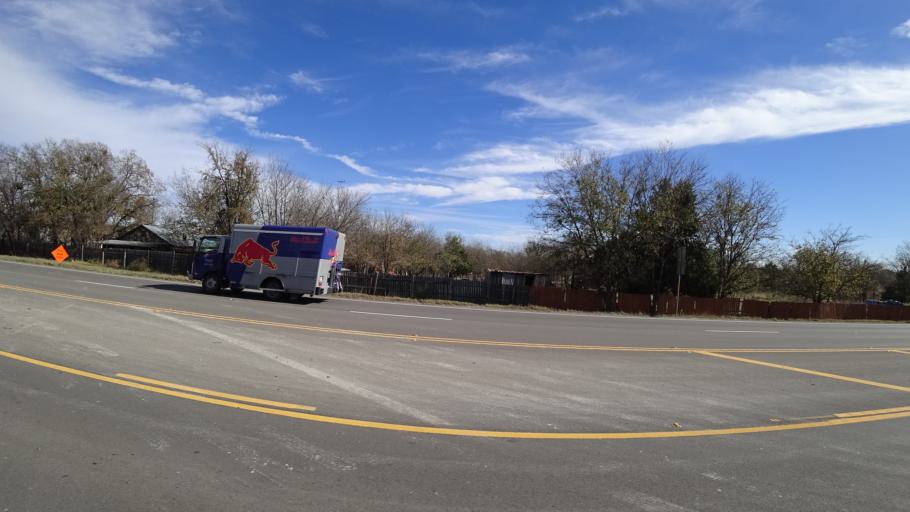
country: US
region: Texas
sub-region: Travis County
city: Onion Creek
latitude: 30.1065
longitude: -97.6947
